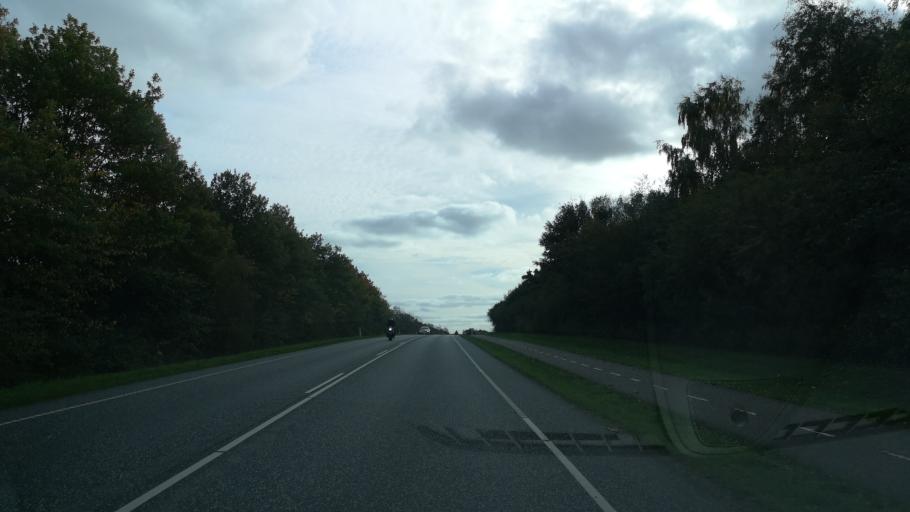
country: DK
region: Central Jutland
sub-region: Holstebro Kommune
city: Holstebro
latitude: 56.3257
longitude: 8.6102
